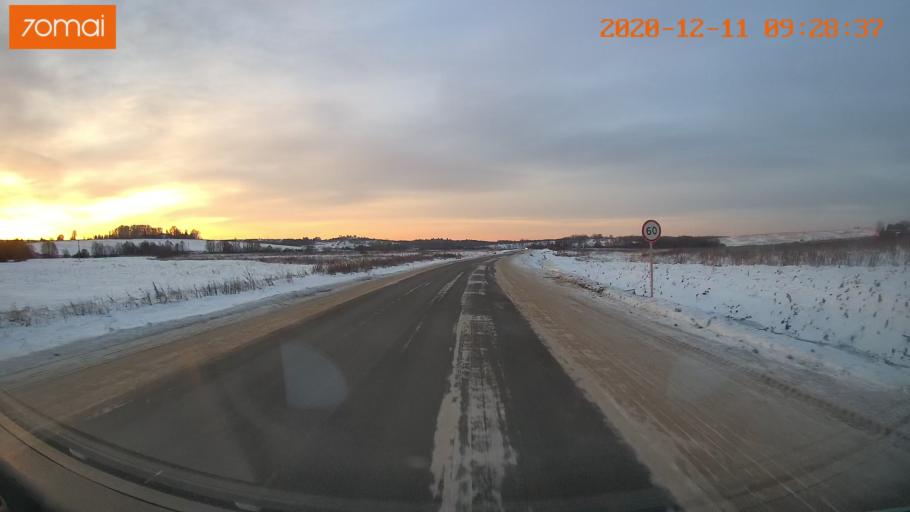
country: RU
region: Vologda
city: Vologda
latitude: 59.1511
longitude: 40.0073
